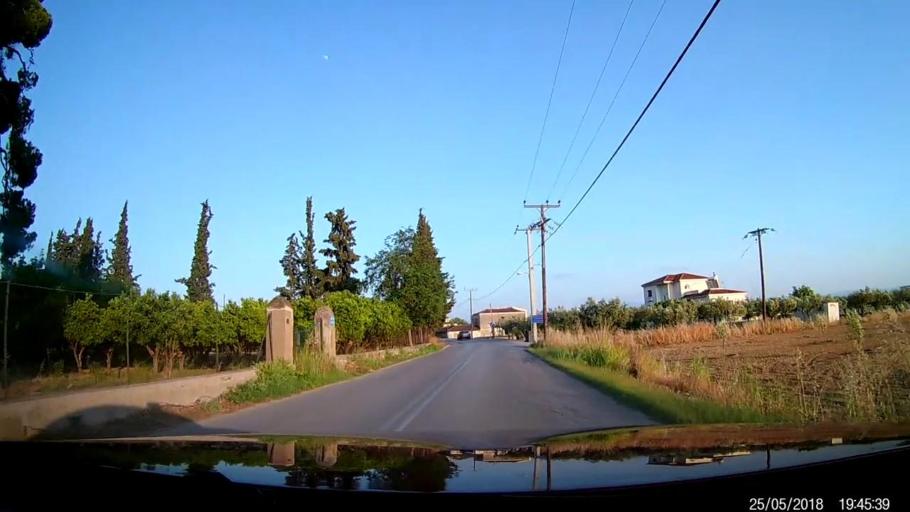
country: GR
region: Central Greece
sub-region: Nomos Evvoias
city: Ayios Nikolaos
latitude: 38.4313
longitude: 23.6345
